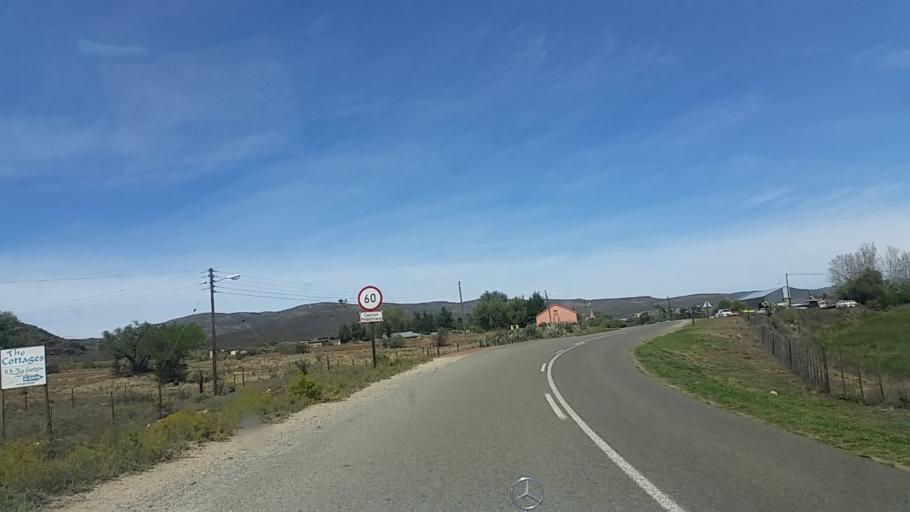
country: ZA
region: Western Cape
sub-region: Eden District Municipality
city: Knysna
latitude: -33.6439
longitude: 23.1381
